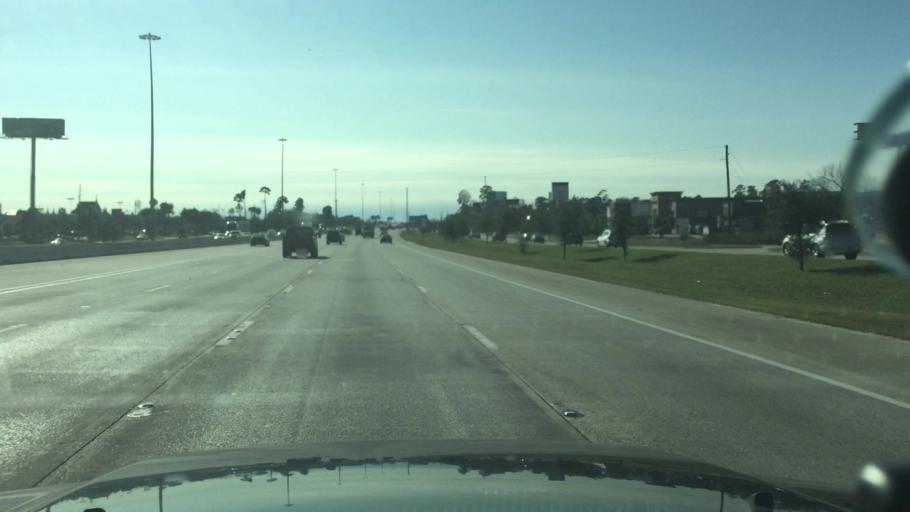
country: US
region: Texas
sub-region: Montgomery County
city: Shenandoah
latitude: 30.1911
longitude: -95.4535
